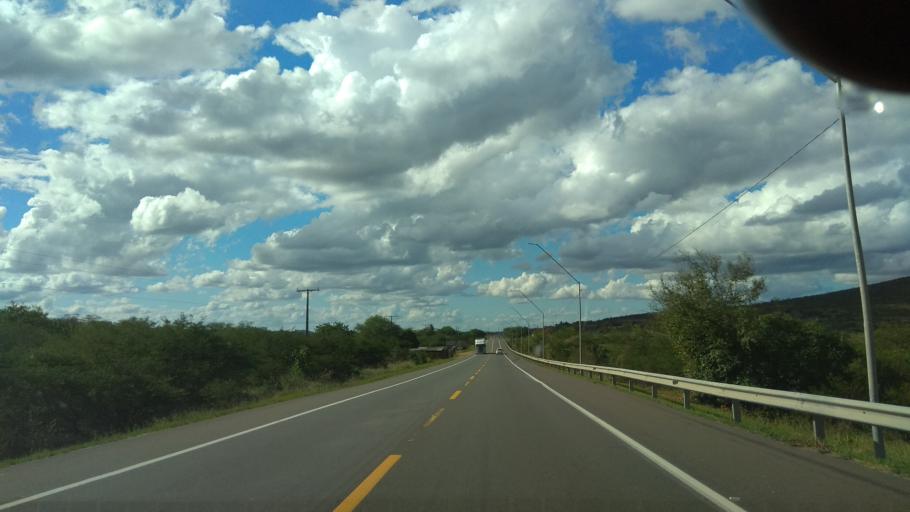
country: BR
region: Bahia
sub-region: Castro Alves
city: Castro Alves
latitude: -12.6354
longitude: -39.5993
